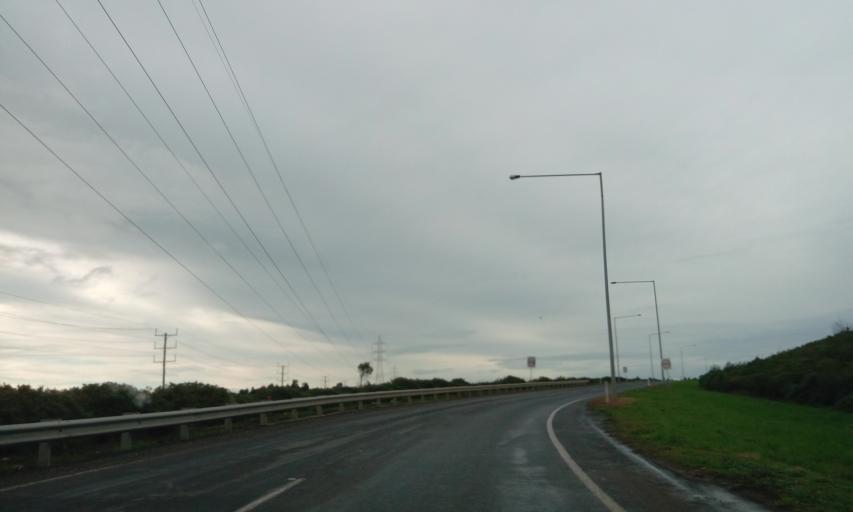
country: AU
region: Victoria
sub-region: Greater Geelong
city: Wandana Heights
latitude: -38.1409
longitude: 144.2947
